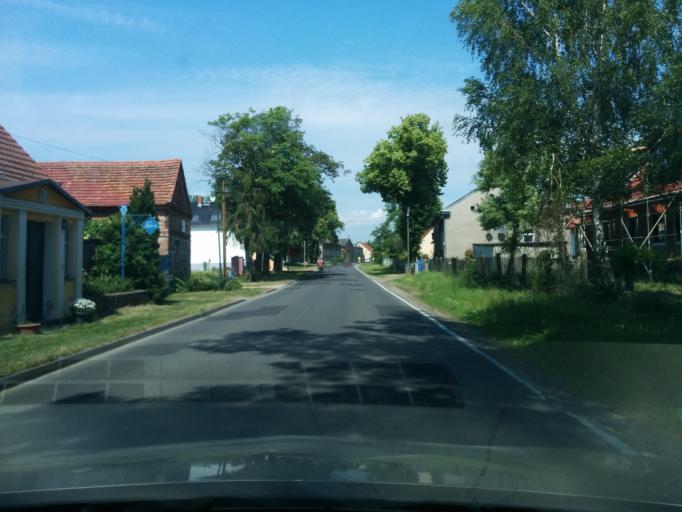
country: DE
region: Brandenburg
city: Ahrensfelde
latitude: 52.6238
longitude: 13.5757
